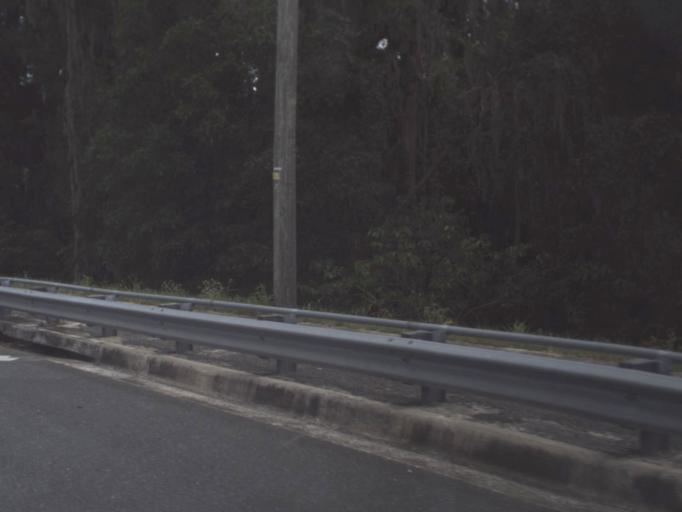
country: US
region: Florida
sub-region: Marion County
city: Ocala
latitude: 29.1790
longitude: -82.1439
